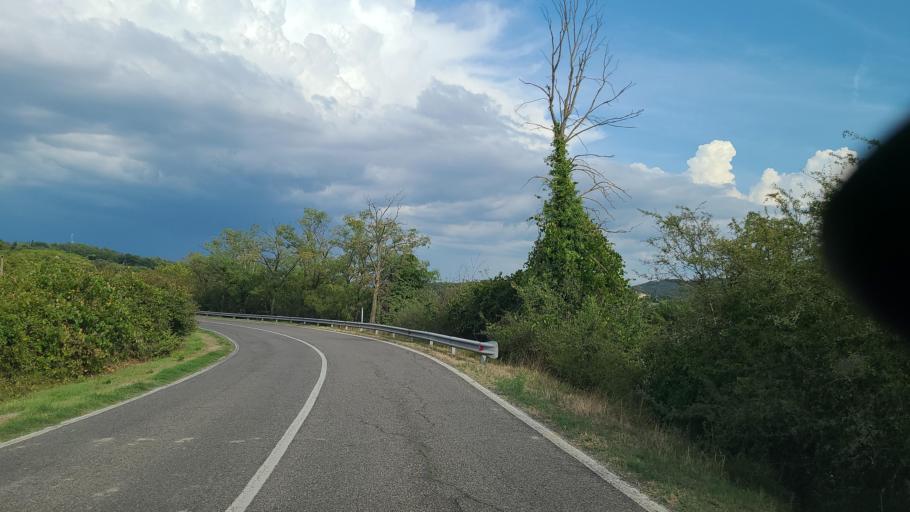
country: IT
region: Tuscany
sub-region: Province of Florence
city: Gambassi Terme
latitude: 43.4849
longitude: 10.9671
